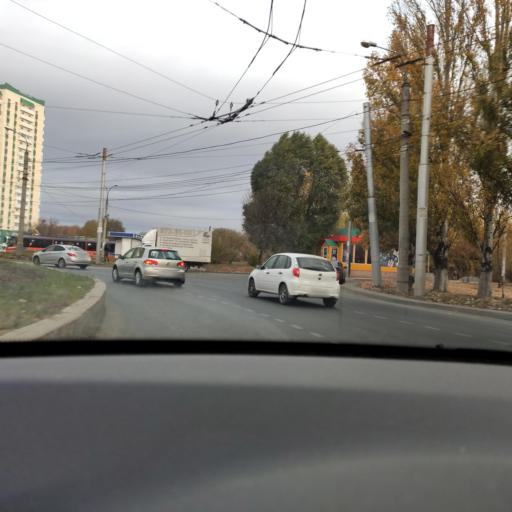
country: RU
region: Samara
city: Samara
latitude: 53.2125
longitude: 50.2138
